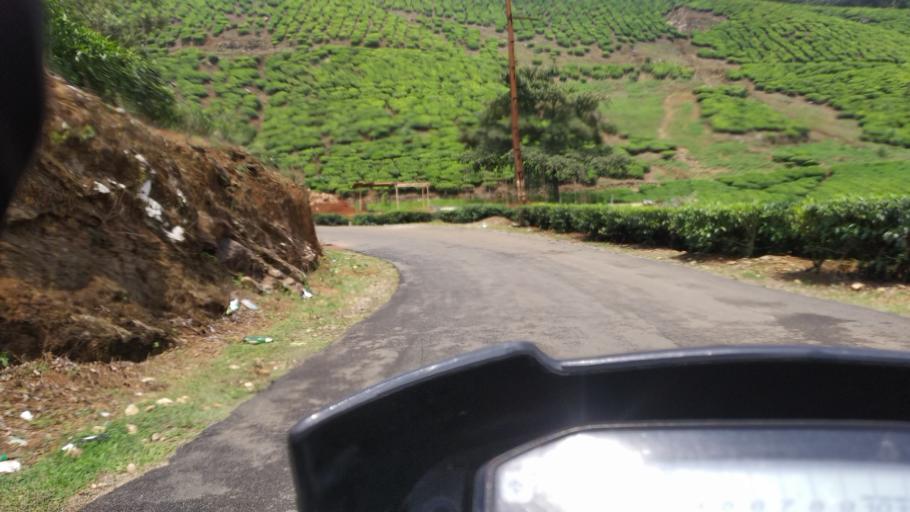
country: IN
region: Kerala
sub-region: Kottayam
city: Erattupetta
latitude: 9.6260
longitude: 76.9745
